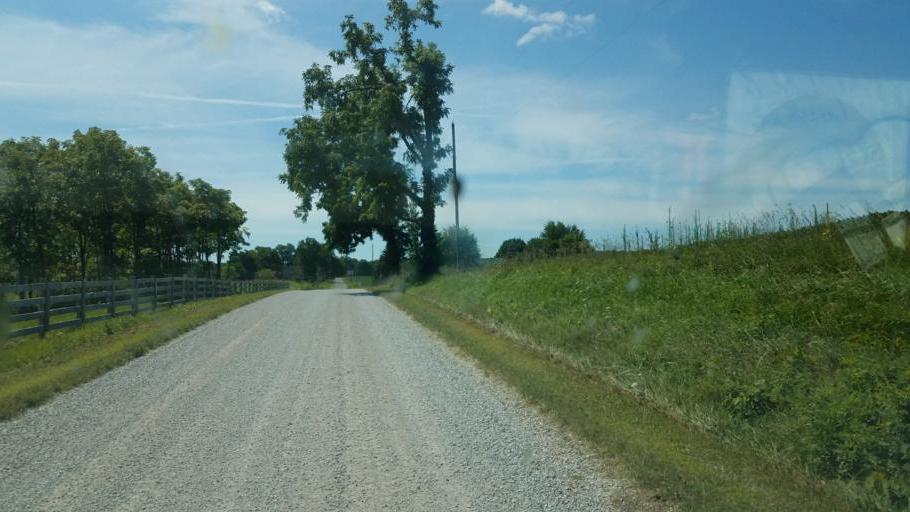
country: US
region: Ohio
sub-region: Knox County
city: Centerburg
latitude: 40.4407
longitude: -82.7272
